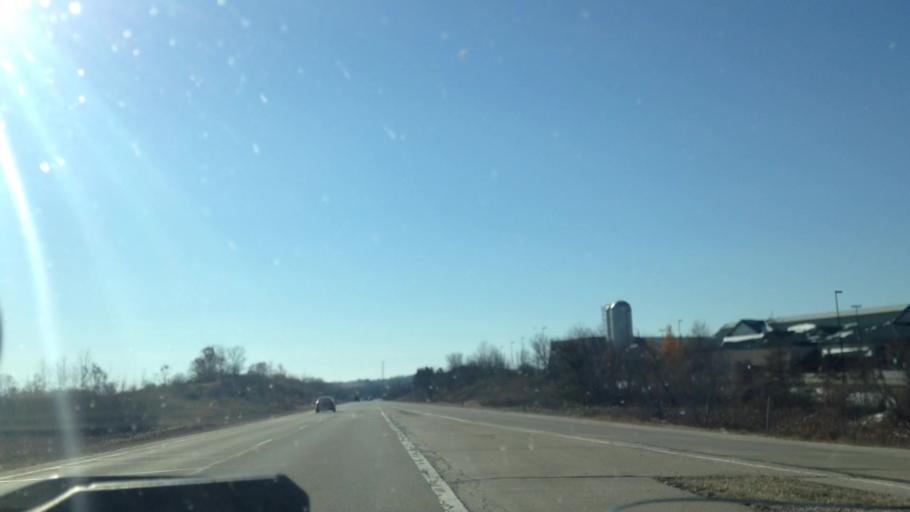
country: US
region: Wisconsin
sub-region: Washington County
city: Richfield
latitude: 43.2808
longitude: -88.1862
